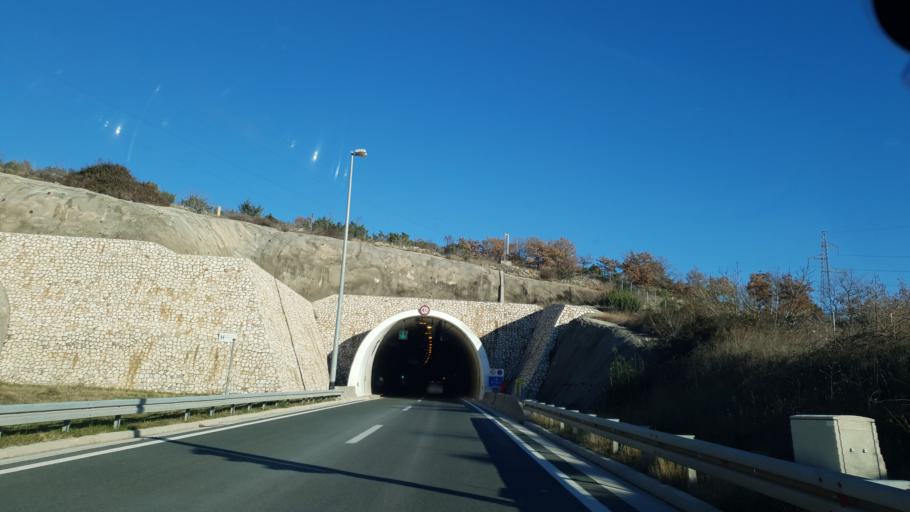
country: HR
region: Splitsko-Dalmatinska
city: Dugopolje
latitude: 43.6046
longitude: 16.5861
